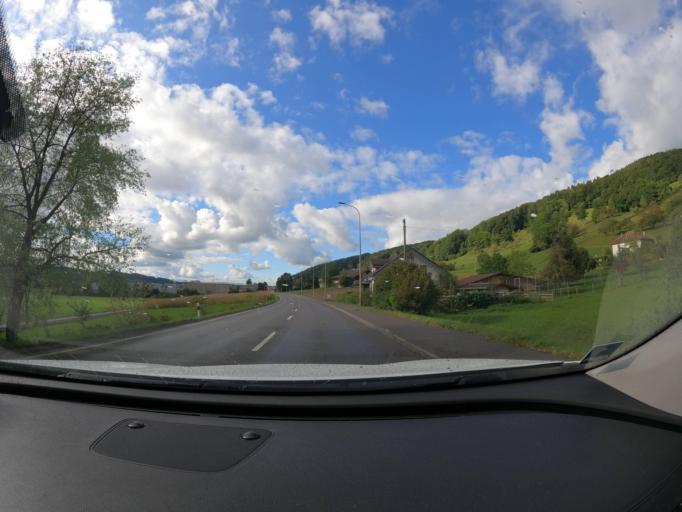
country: CH
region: Aargau
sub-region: Bezirk Kulm
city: Reinach
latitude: 47.2682
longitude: 8.1753
